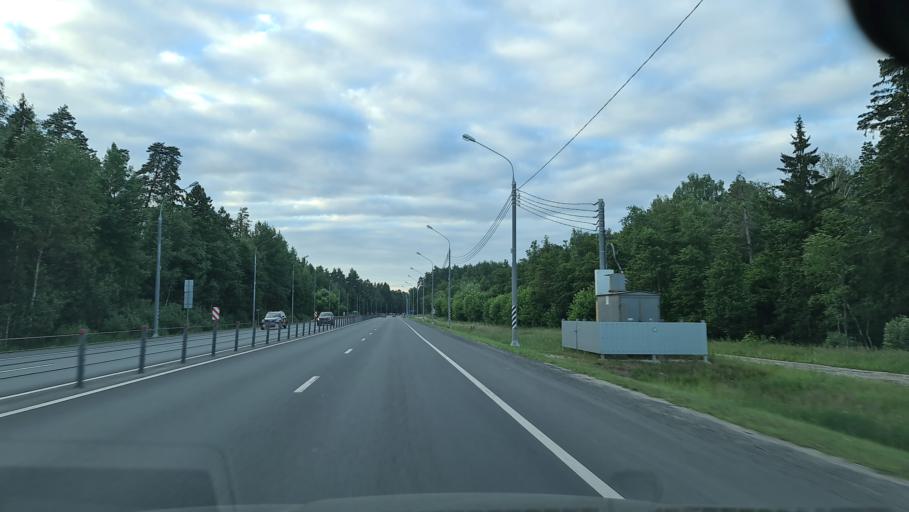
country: RU
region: Moskovskaya
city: Malaya Dubna
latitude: 55.8592
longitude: 38.9624
